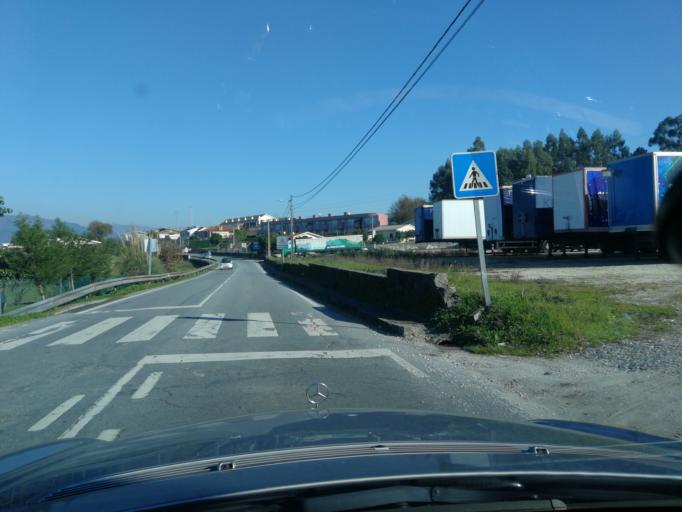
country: PT
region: Braga
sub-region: Braga
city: Adaufe
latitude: 41.6116
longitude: -8.4190
